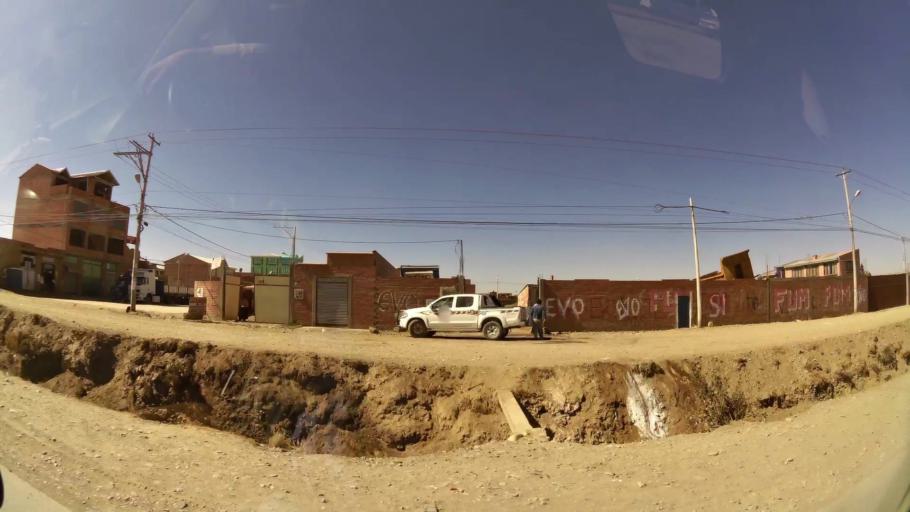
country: BO
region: La Paz
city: La Paz
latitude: -16.5575
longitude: -68.2112
